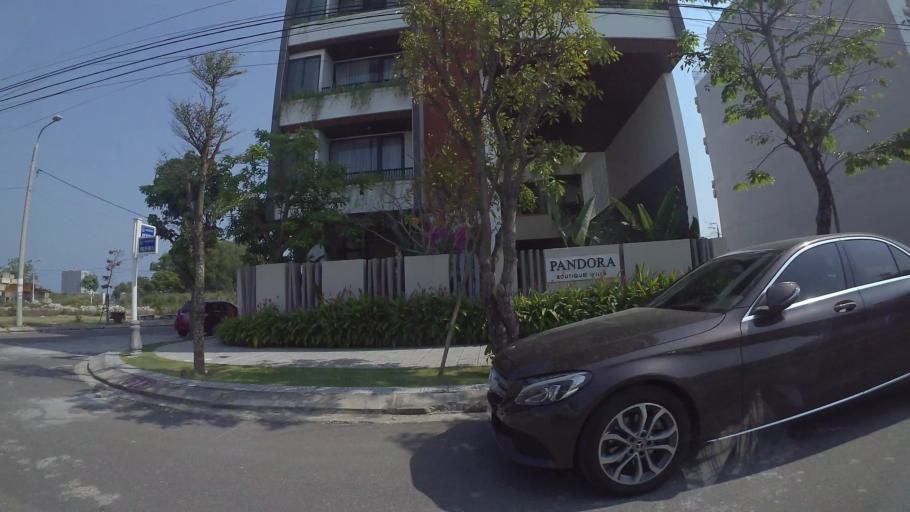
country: VN
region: Da Nang
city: Ngu Hanh Son
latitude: 16.0373
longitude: 108.2474
